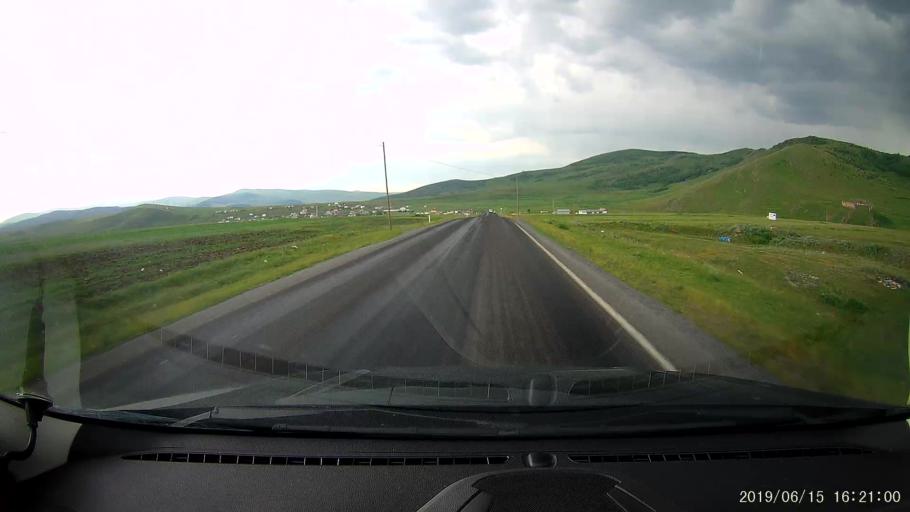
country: TR
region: Ardahan
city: Hanak
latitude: 41.2045
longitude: 42.8464
